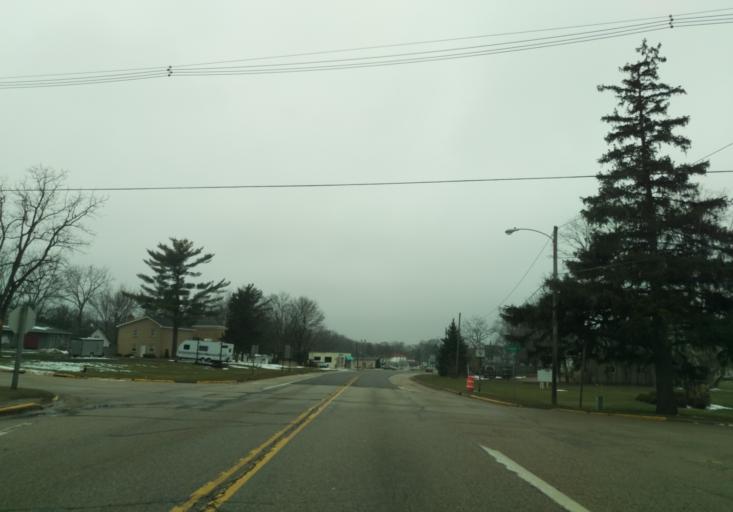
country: US
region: Wisconsin
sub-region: Dane County
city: Mazomanie
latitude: 43.1722
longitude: -89.7909
